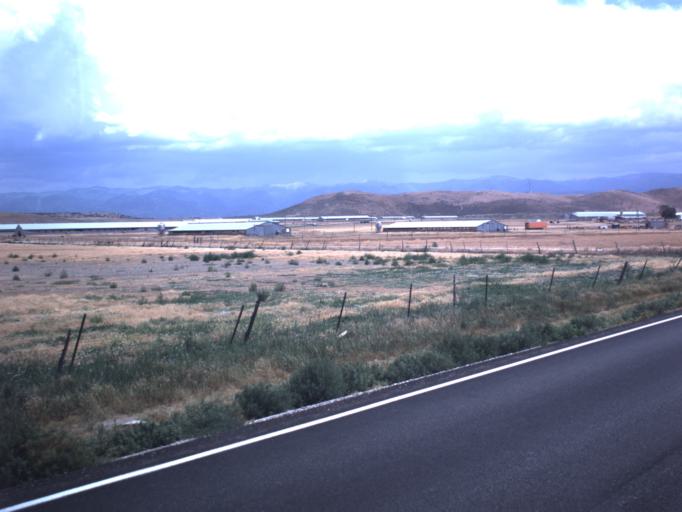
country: US
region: Utah
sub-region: Sanpete County
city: Moroni
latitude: 39.5650
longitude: -111.6044
